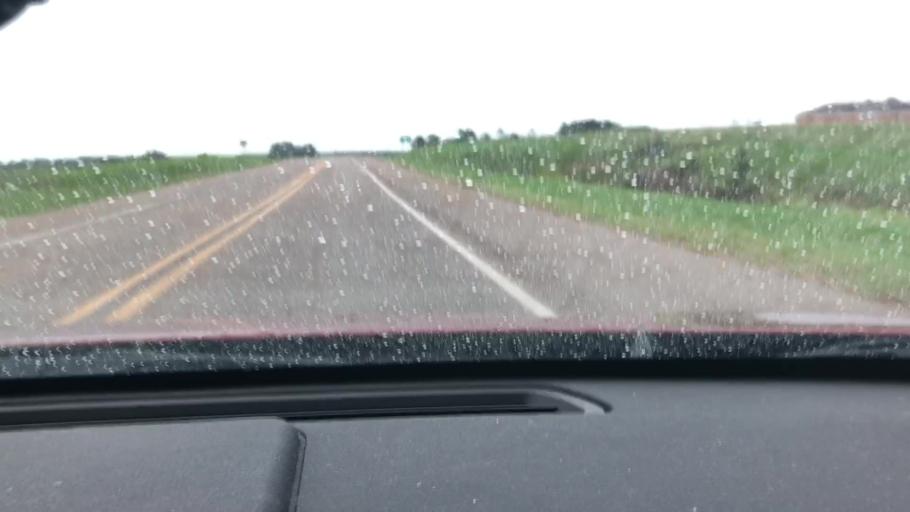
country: US
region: Arkansas
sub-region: Columbia County
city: Magnolia
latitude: 33.2971
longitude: -93.2409
